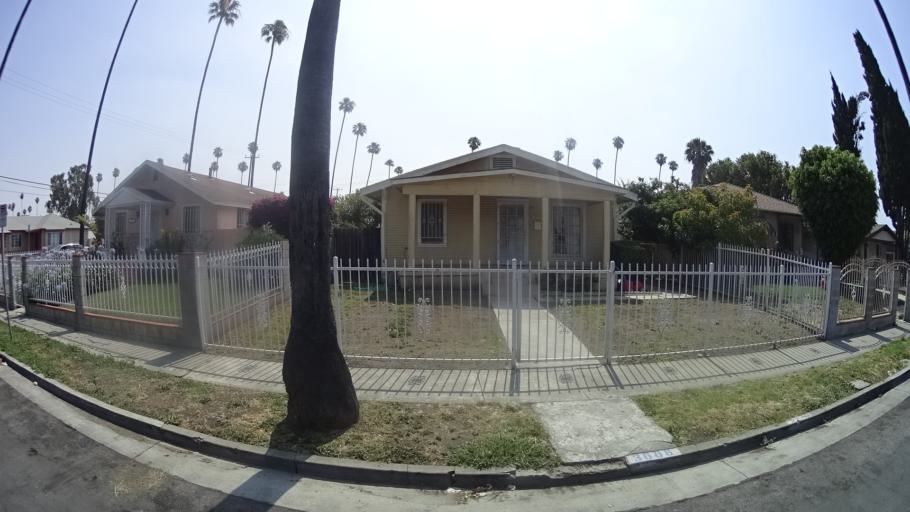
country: US
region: California
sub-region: Los Angeles County
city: View Park-Windsor Hills
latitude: 34.0227
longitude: -118.3272
